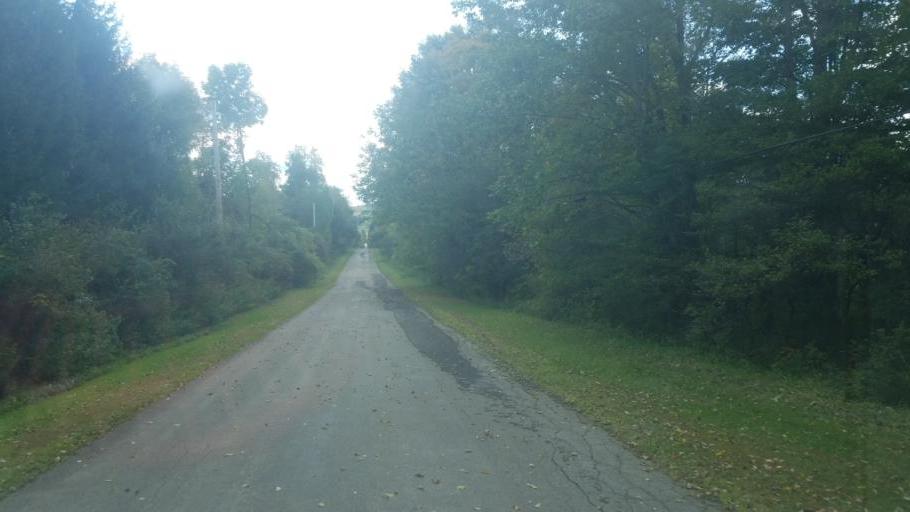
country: US
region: New York
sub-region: Cattaraugus County
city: Franklinville
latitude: 42.2221
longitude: -78.4145
